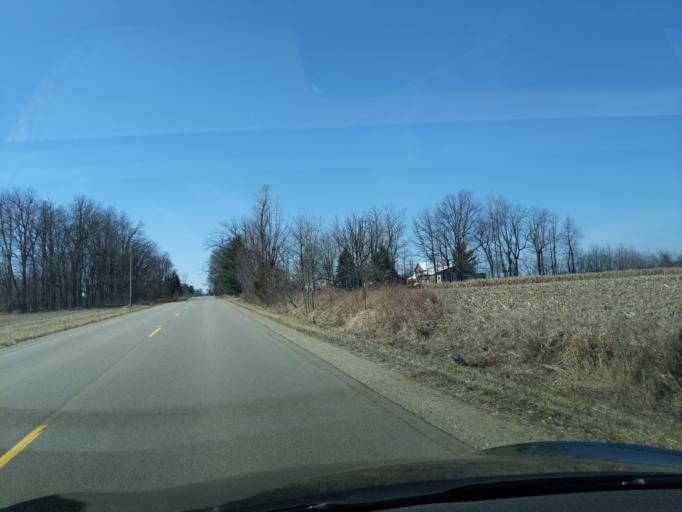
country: US
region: Michigan
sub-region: Eaton County
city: Grand Ledge
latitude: 42.7266
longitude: -84.8407
